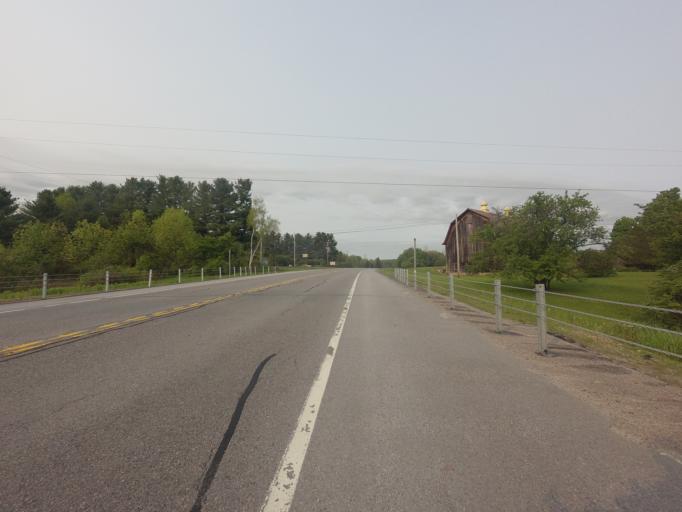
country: US
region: New York
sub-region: Jefferson County
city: Carthage
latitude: 44.0377
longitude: -75.5739
